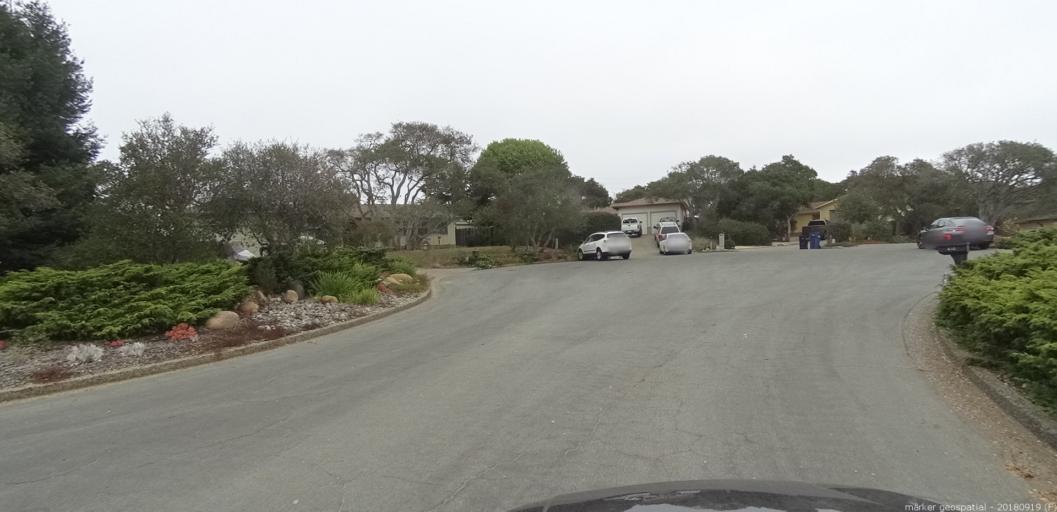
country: US
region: California
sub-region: Monterey County
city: Prunedale
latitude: 36.7820
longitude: -121.7024
